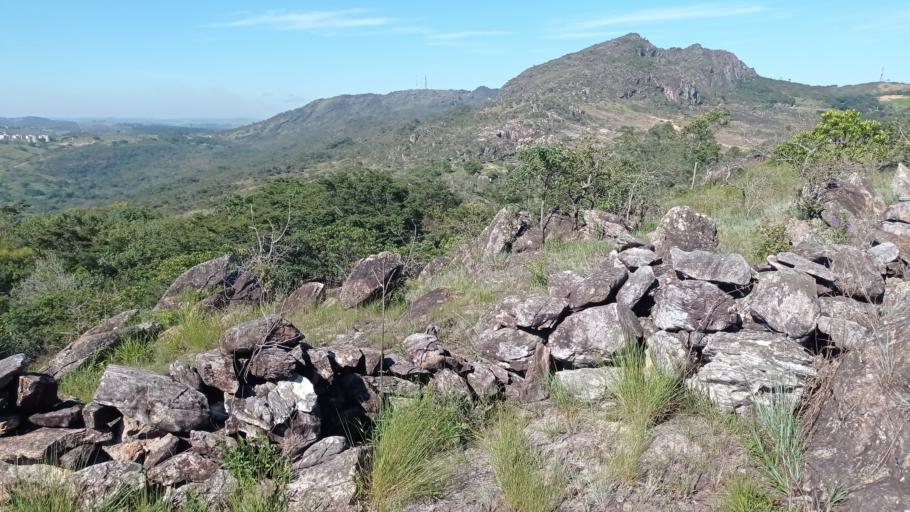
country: BR
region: Minas Gerais
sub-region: Sao Joao Del Rei
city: Sao Joao del Rei
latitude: -21.1378
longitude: -44.2863
